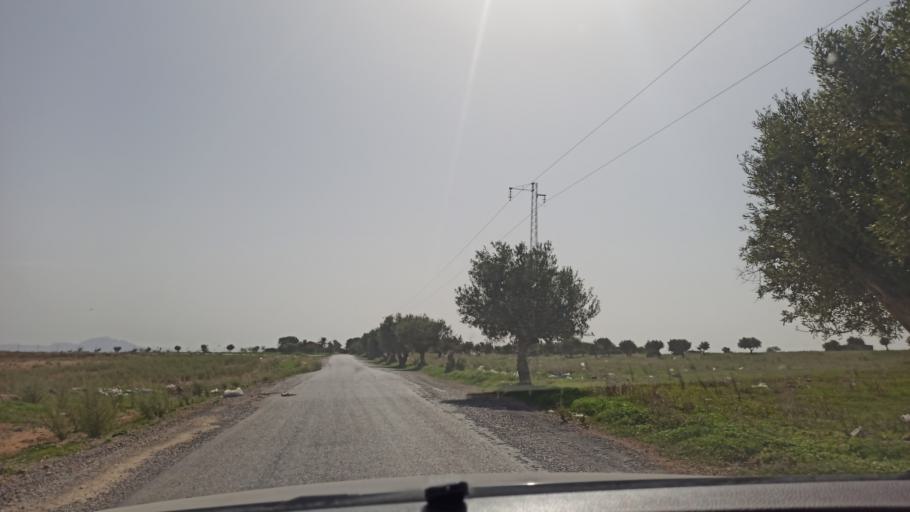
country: TN
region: Manouba
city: Manouba
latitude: 36.7347
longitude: 10.0861
